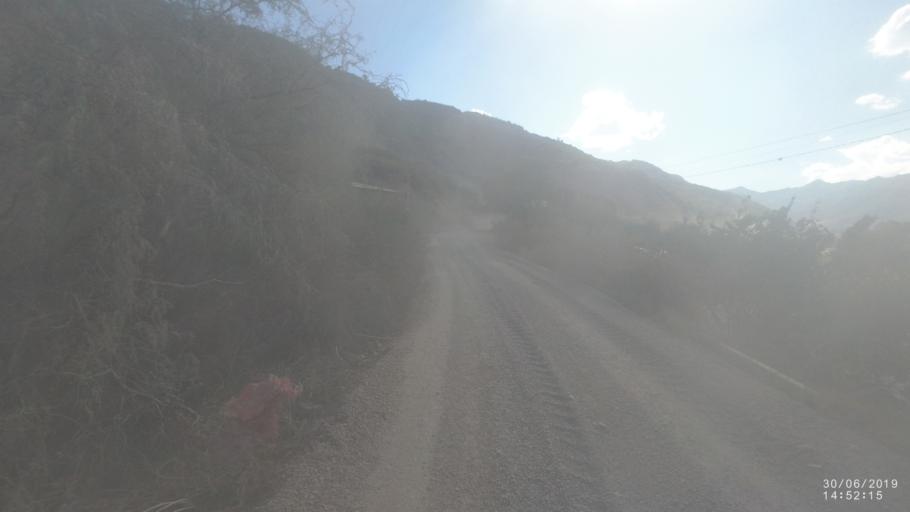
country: BO
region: Cochabamba
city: Irpa Irpa
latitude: -17.7695
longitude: -66.3454
